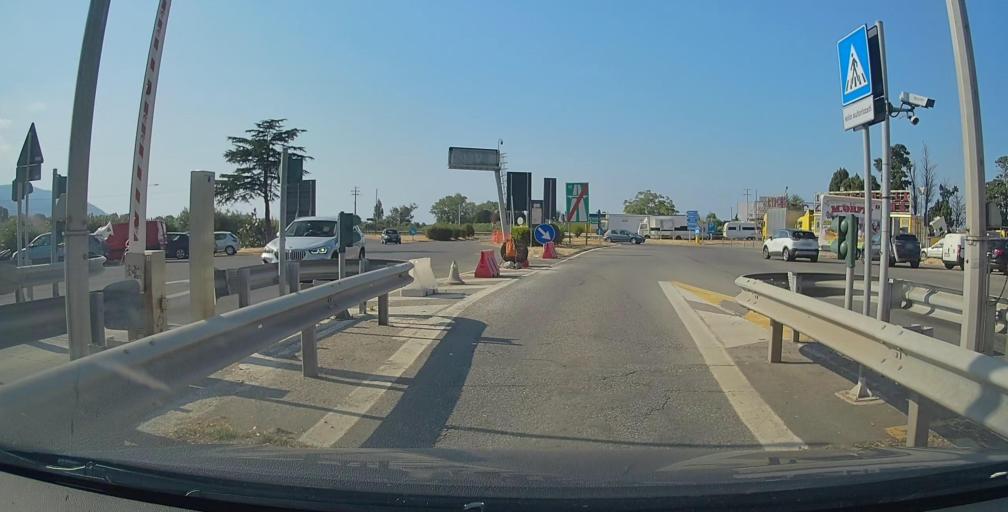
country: IT
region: Sicily
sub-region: Messina
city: Patti
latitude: 38.1455
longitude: 14.9994
